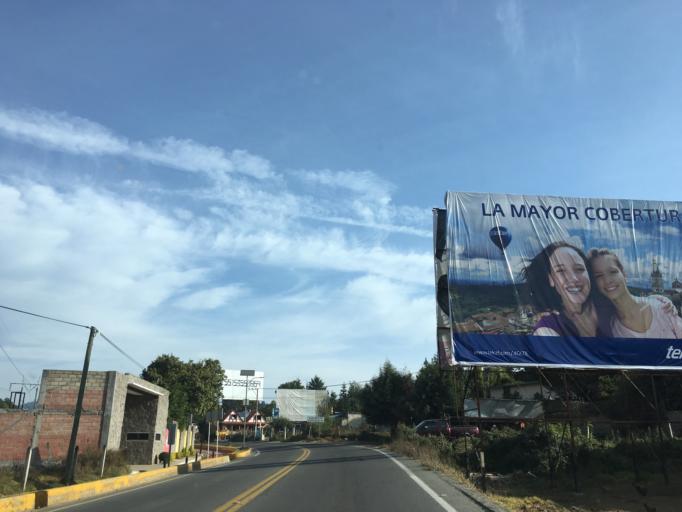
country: MX
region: Mexico
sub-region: Valle de Bravo
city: Colonia Rincon Villa del Valle
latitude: 19.1921
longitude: -100.1002
